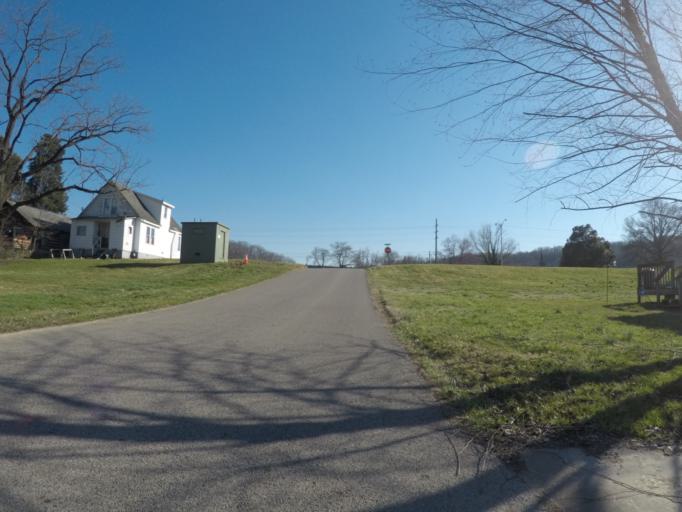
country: US
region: Ohio
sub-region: Lawrence County
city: Burlington
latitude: 38.3997
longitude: -82.5174
